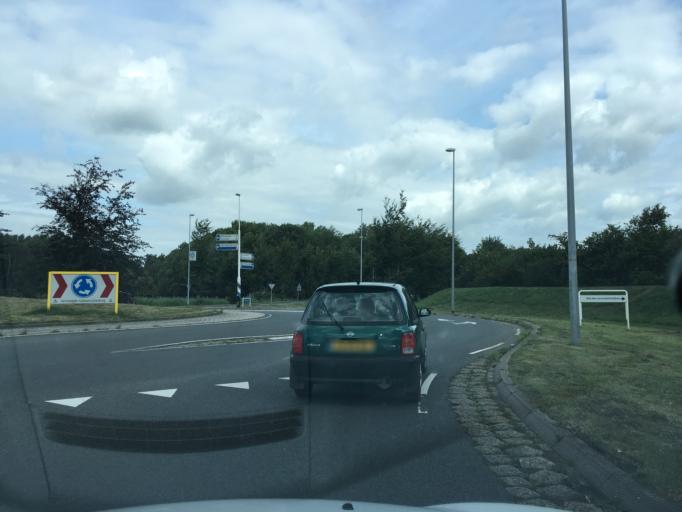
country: NL
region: Flevoland
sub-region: Gemeente Almere
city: Almere Stad
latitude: 52.3770
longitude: 5.2341
